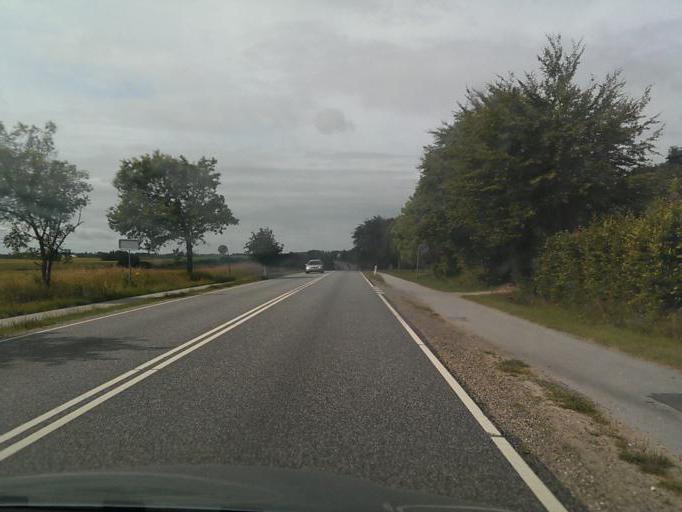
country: DK
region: North Denmark
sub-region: Hjorring Kommune
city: Hjorring
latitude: 57.4561
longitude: 9.9260
